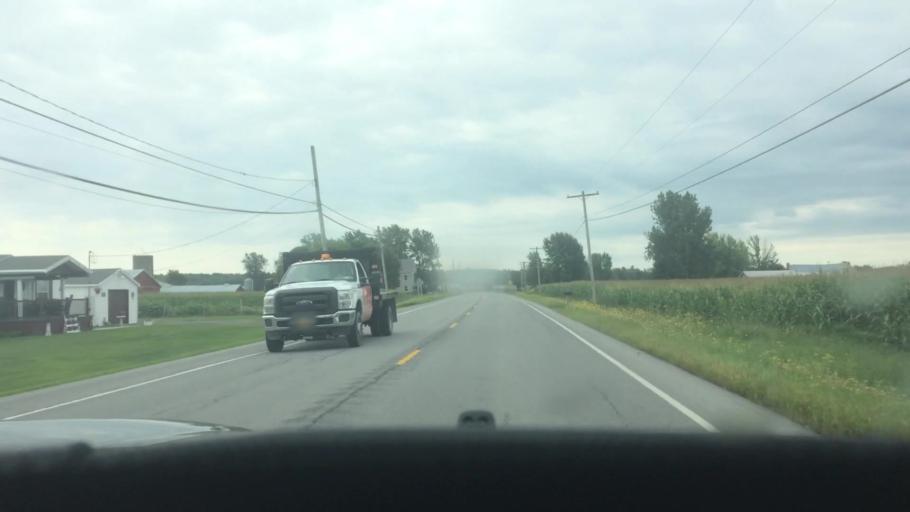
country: US
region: New York
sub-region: St. Lawrence County
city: Ogdensburg
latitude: 44.6669
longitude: -75.4687
